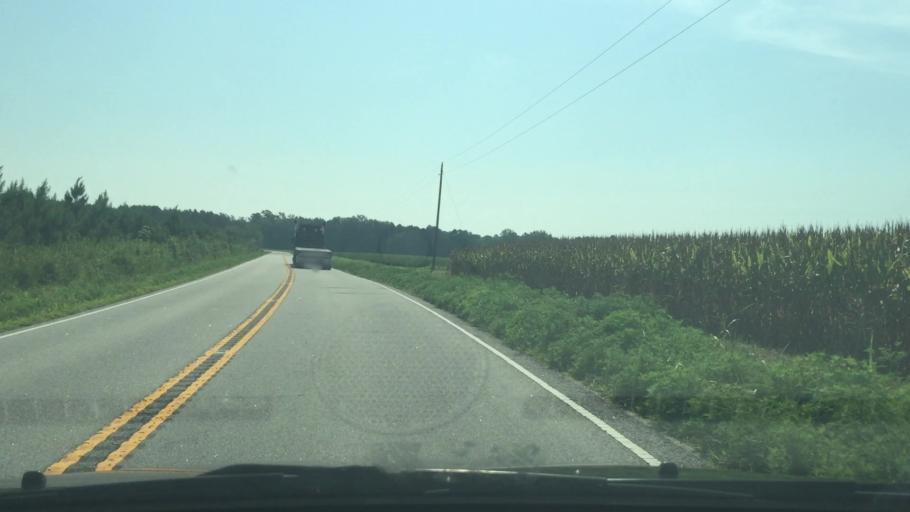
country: US
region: Virginia
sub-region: Sussex County
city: Sussex
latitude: 36.9774
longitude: -77.2263
